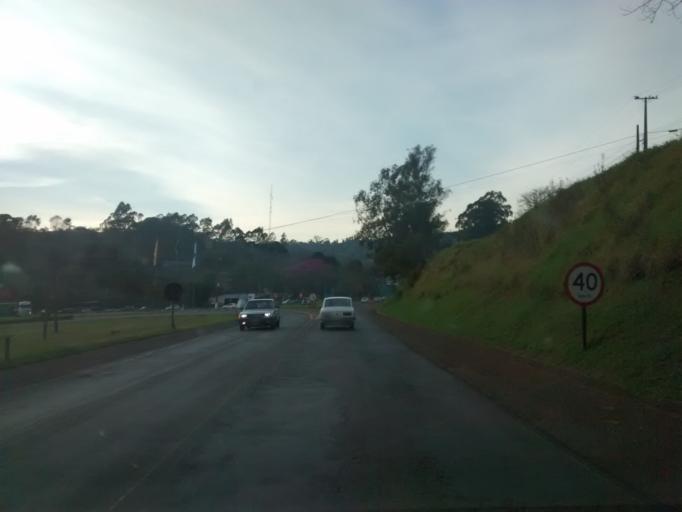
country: BR
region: Parana
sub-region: Francisco Beltrao
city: Francisco Beltrao
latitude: -26.1144
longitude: -53.0432
